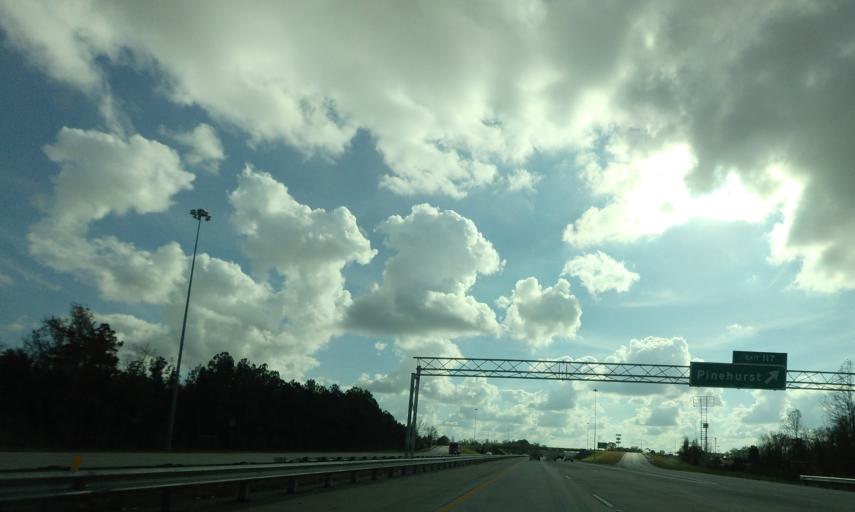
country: US
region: Georgia
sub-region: Dooly County
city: Unadilla
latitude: 32.1946
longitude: -83.7474
